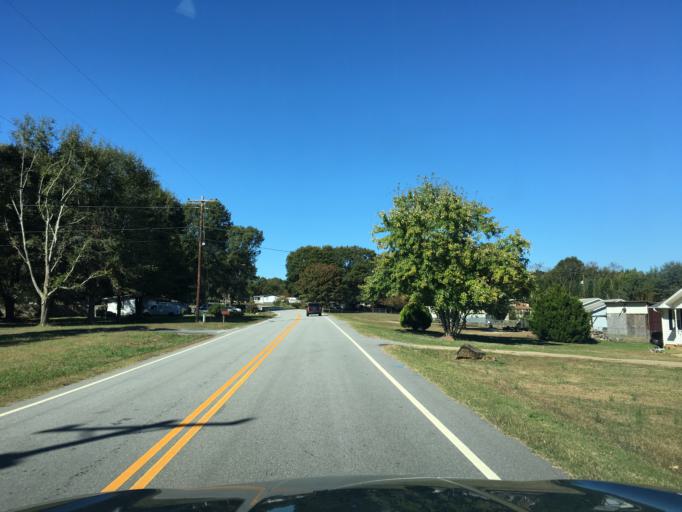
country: US
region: South Carolina
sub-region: Spartanburg County
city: Wellford
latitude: 34.8670
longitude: -82.0965
